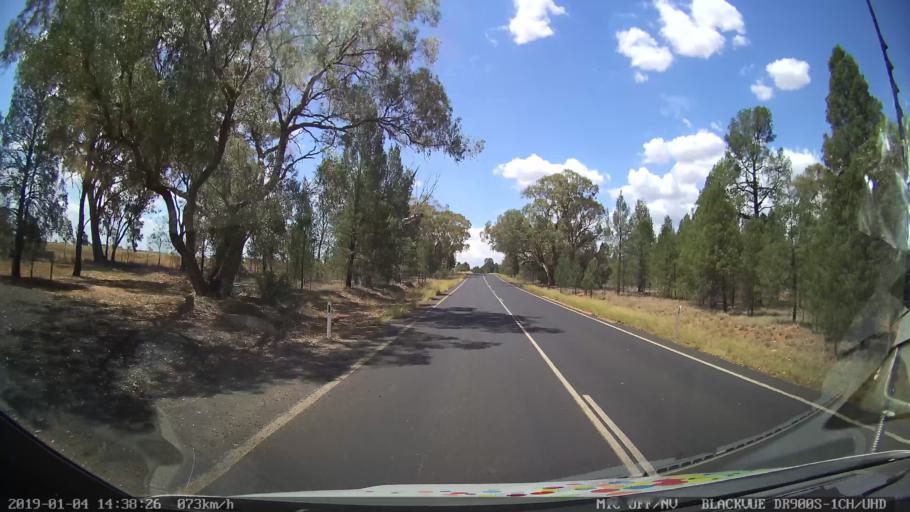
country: AU
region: New South Wales
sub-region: Dubbo Municipality
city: Dubbo
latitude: -32.1758
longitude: 148.6299
